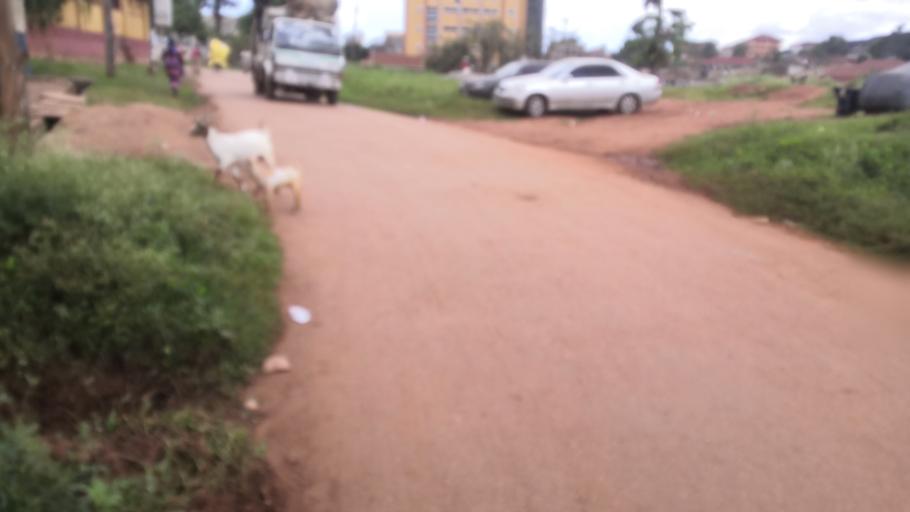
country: UG
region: Central Region
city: Kampala Central Division
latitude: 0.3306
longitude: 32.5620
